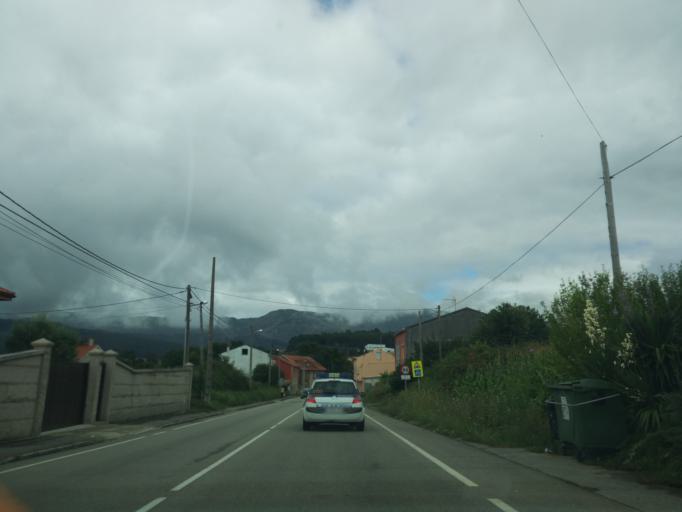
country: ES
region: Galicia
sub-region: Provincia da Coruna
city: Boiro
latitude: 42.6455
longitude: -8.8737
